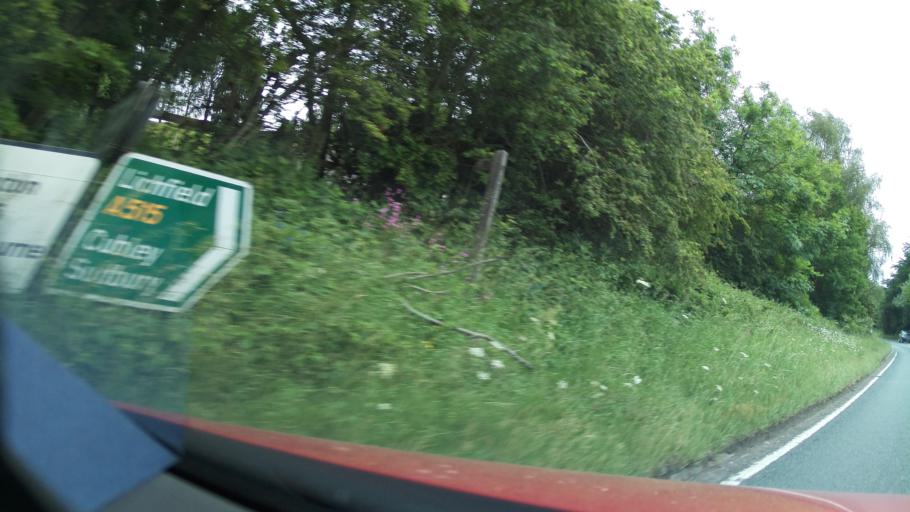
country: GB
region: England
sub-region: Staffordshire
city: Mayfield
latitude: 53.0015
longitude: -1.7514
